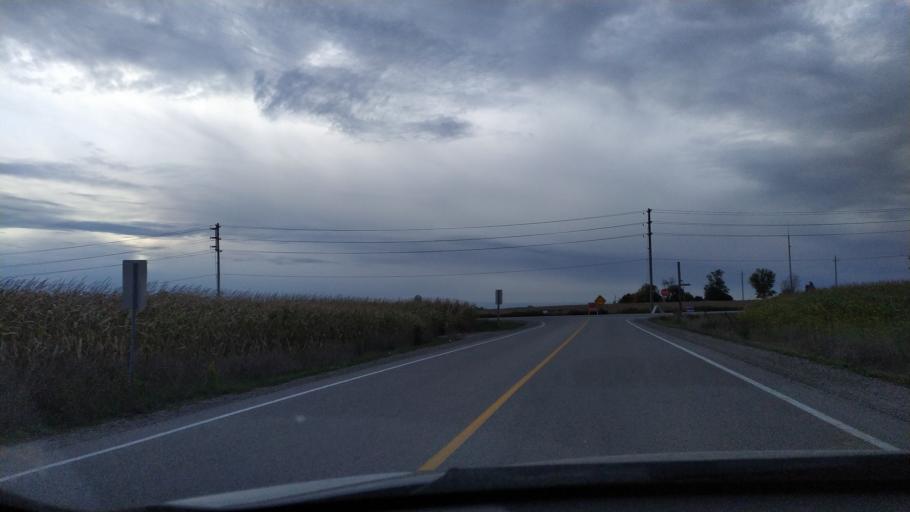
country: CA
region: Ontario
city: Waterloo
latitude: 43.5011
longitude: -80.6215
